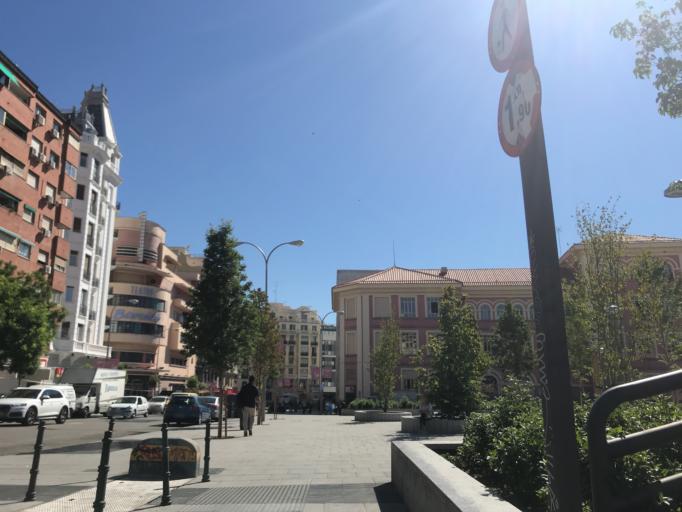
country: ES
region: Madrid
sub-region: Provincia de Madrid
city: Chamberi
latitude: 40.4264
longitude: -3.7006
